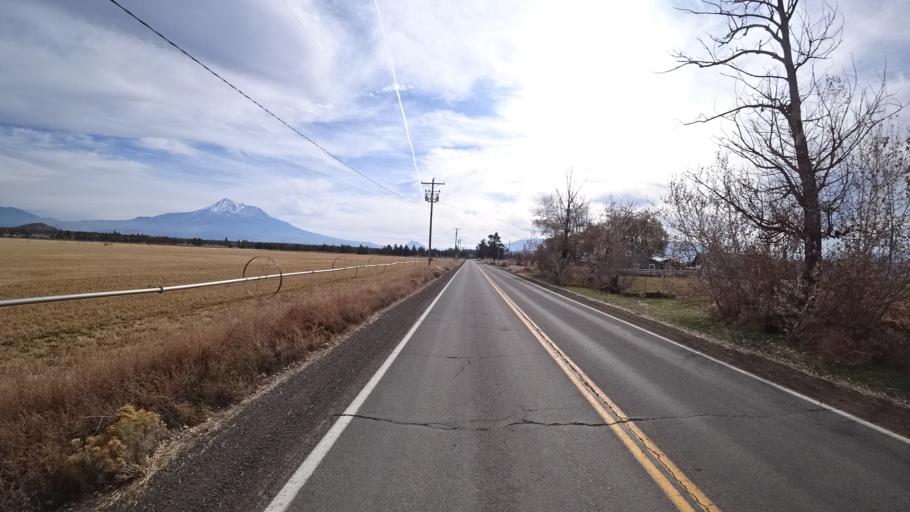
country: US
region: California
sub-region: Siskiyou County
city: Montague
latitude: 41.6155
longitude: -122.3996
